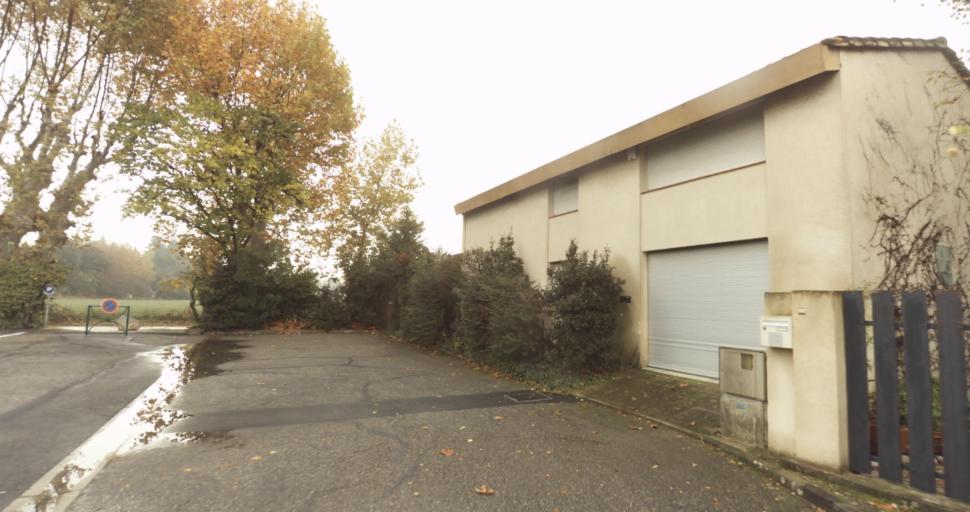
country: FR
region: Provence-Alpes-Cote d'Azur
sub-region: Departement des Bouches-du-Rhone
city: Rognonas
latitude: 43.9011
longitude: 4.8098
